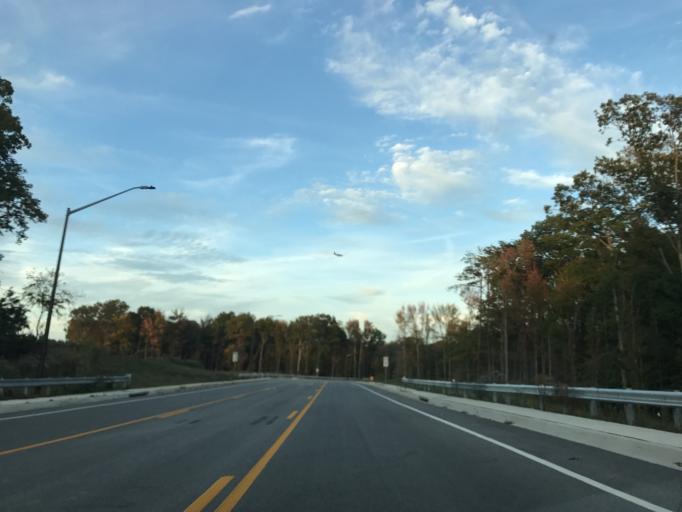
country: US
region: Maryland
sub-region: Anne Arundel County
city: Jessup
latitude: 39.1673
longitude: -76.7665
